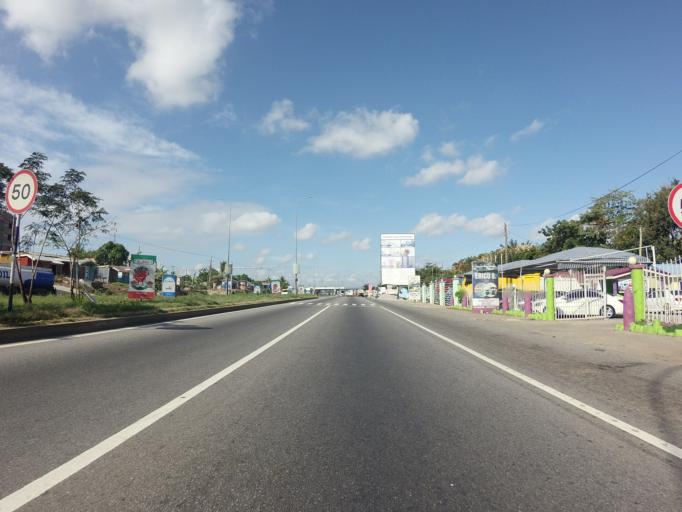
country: GH
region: Central
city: Kasoa
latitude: 5.5488
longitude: -0.3785
